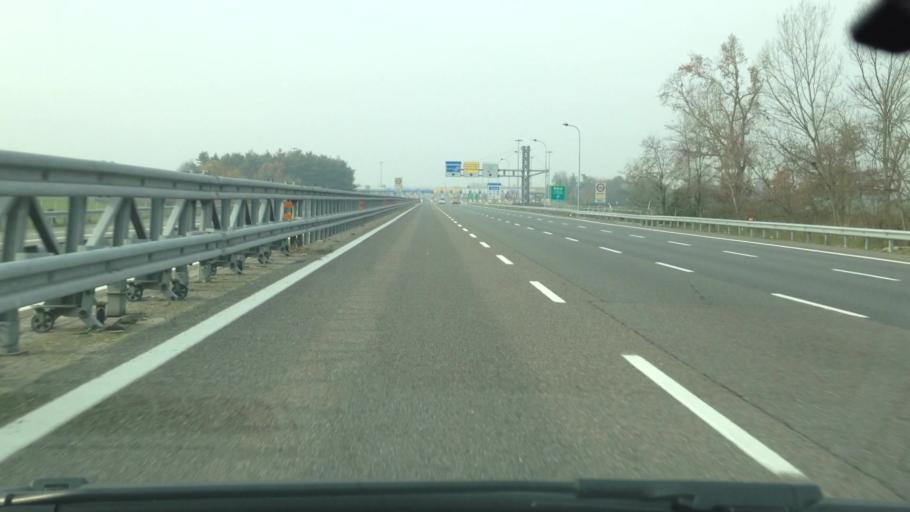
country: IT
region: Piedmont
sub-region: Provincia di Asti
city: Villanova d'Asti
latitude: 44.9523
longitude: 7.9308
